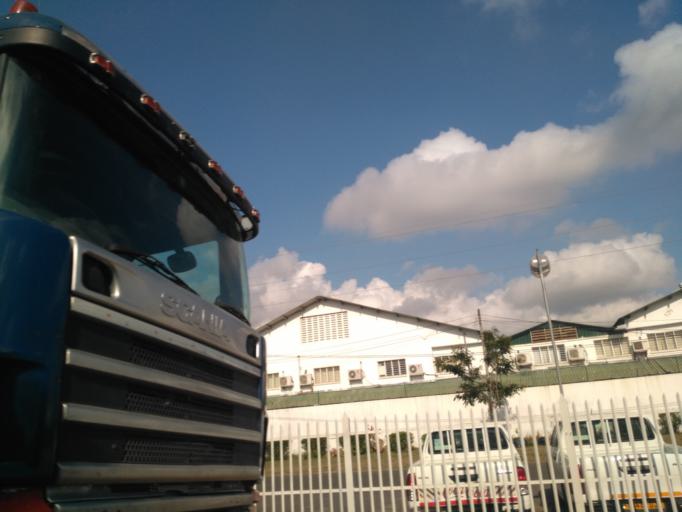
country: TZ
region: Dar es Salaam
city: Magomeni
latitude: -6.7527
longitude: 39.2345
